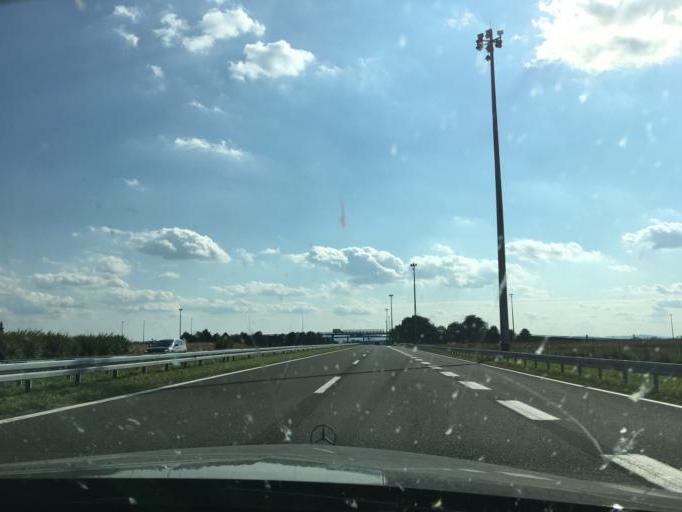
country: HR
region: Medimurska
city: Mala Subotica
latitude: 46.3526
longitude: 16.5350
